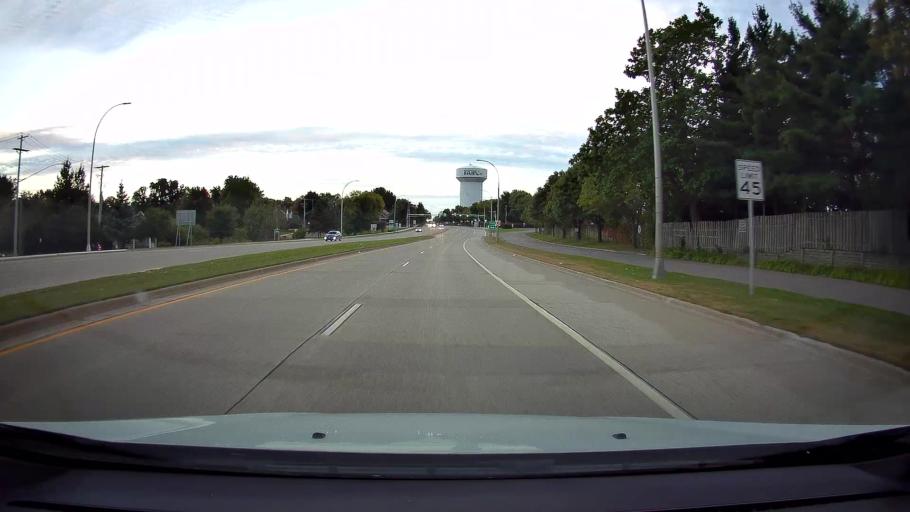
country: US
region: Minnesota
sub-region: Ramsey County
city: Falcon Heights
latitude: 44.9904
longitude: -93.1668
